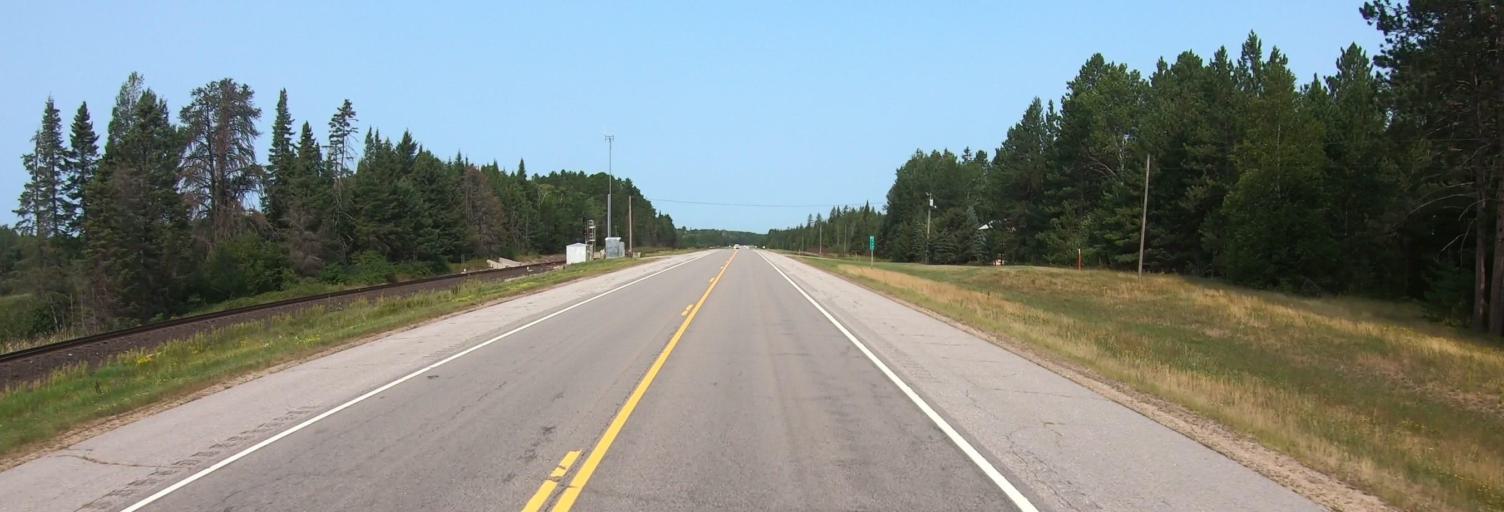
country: US
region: Minnesota
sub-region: Saint Louis County
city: Mountain Iron
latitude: 48.1399
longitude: -92.8565
